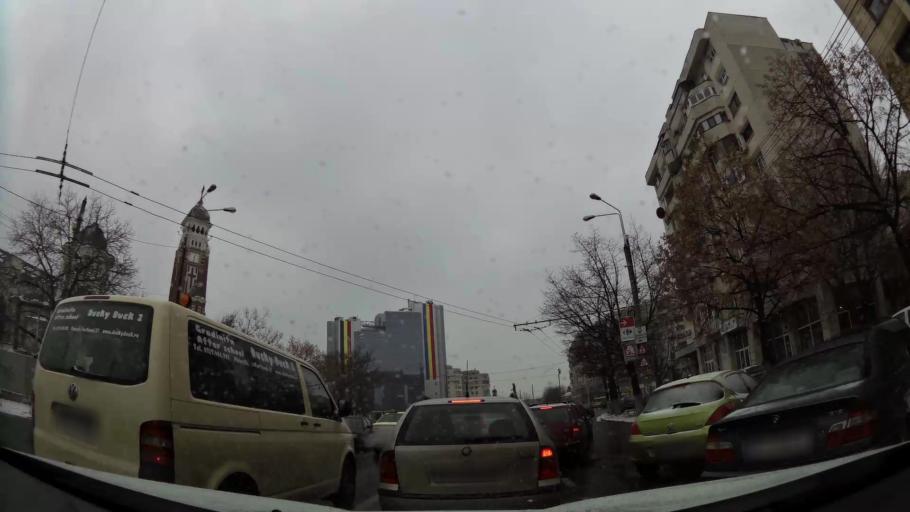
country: RO
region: Prahova
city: Ploiesti
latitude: 44.9440
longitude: 26.0188
